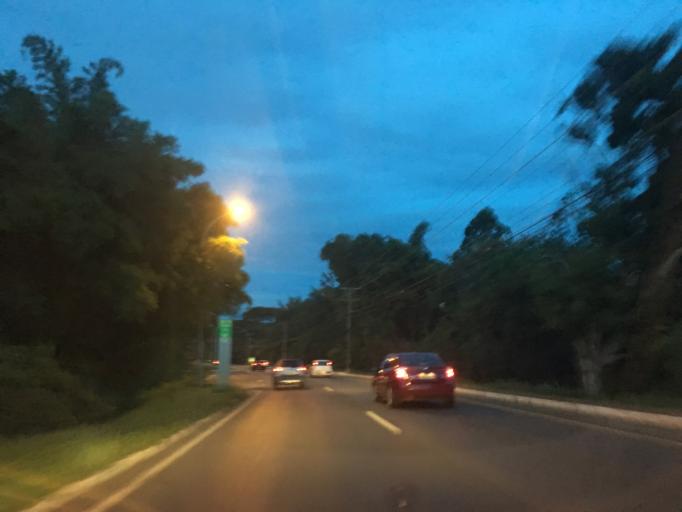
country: BR
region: Federal District
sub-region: Brasilia
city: Brasilia
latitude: -15.8553
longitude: -47.8584
